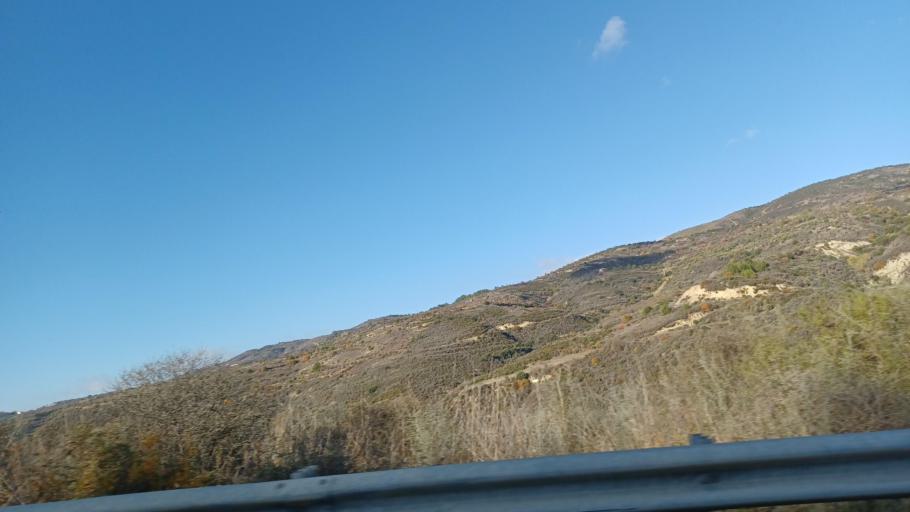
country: CY
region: Limassol
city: Pachna
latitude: 34.8526
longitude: 32.7284
